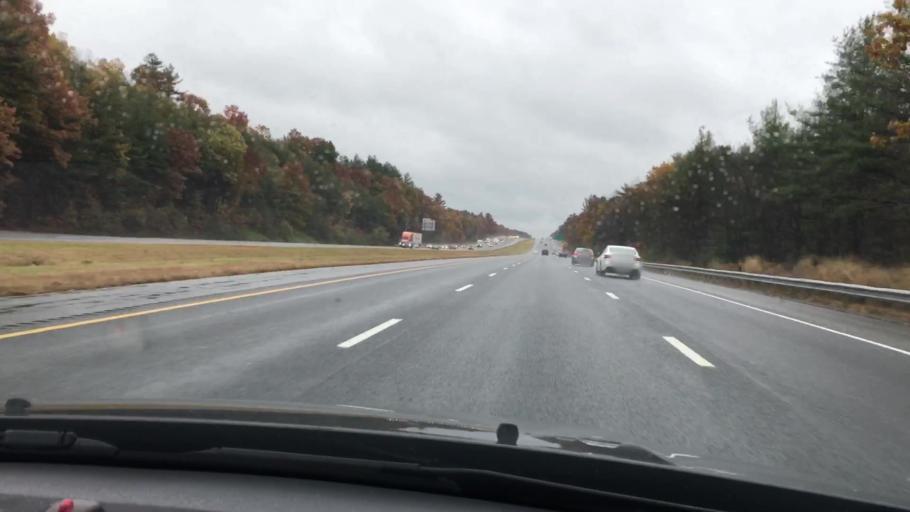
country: US
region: Massachusetts
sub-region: Middlesex County
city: Tyngsboro
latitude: 42.6661
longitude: -71.4346
